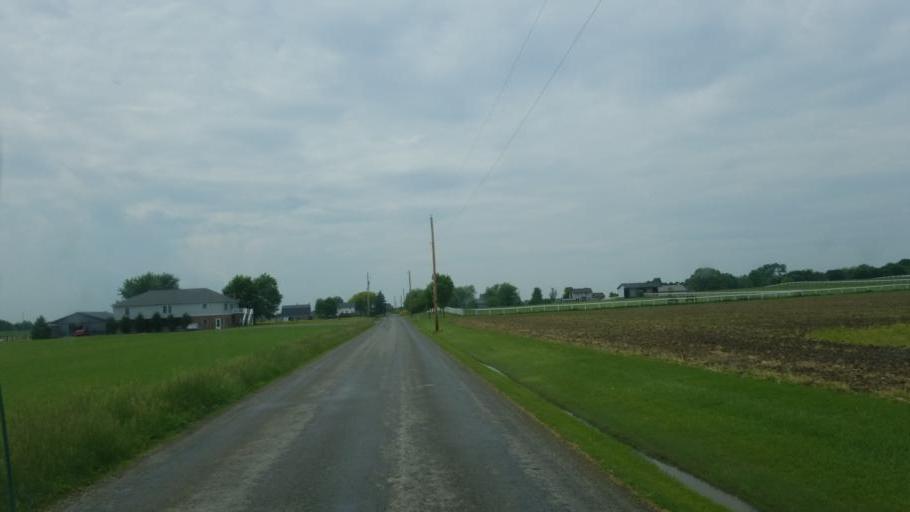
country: US
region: Ohio
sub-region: Wayne County
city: Orrville
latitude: 40.7821
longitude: -81.7703
